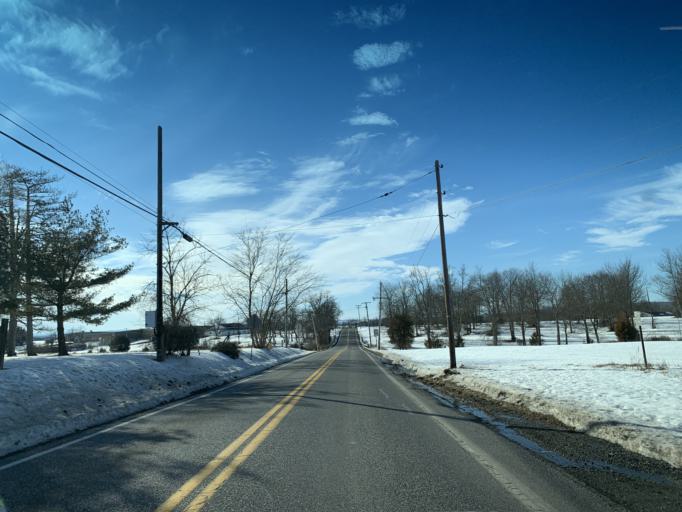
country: US
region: Pennsylvania
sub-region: York County
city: Dillsburg
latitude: 40.0530
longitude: -76.9697
